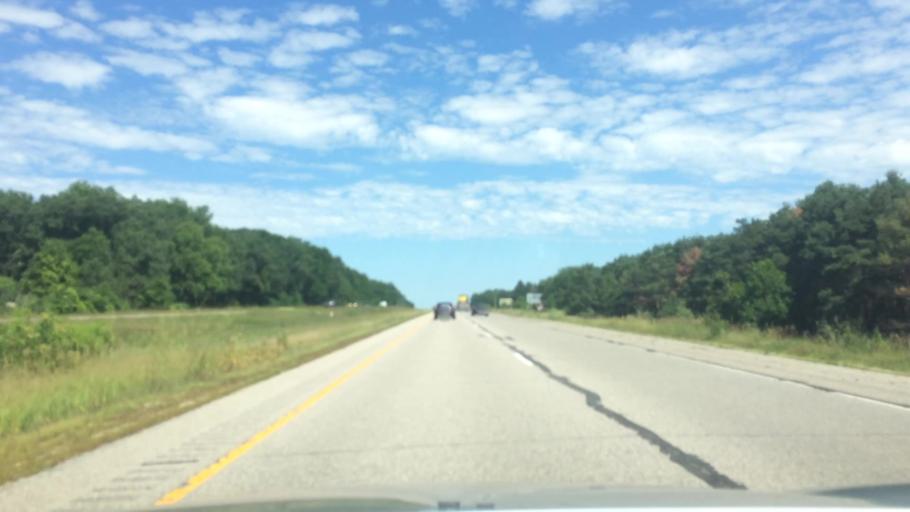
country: US
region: Wisconsin
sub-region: Marquette County
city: Westfield
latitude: 43.7209
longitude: -89.4785
